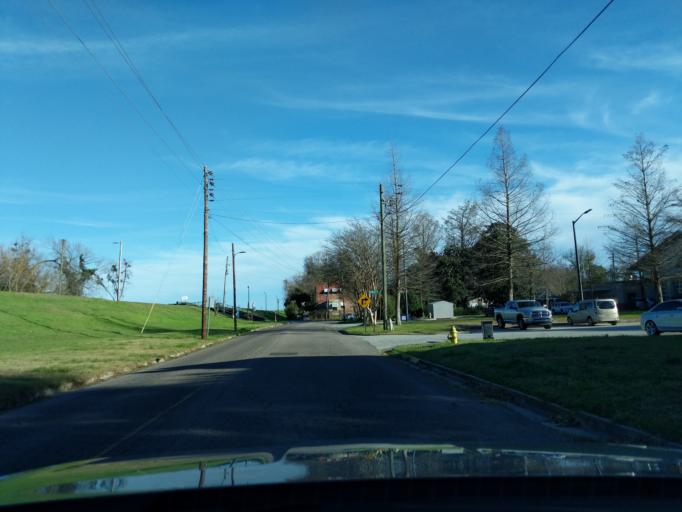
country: US
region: Georgia
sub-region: Richmond County
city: Augusta
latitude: 33.4706
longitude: -81.9487
